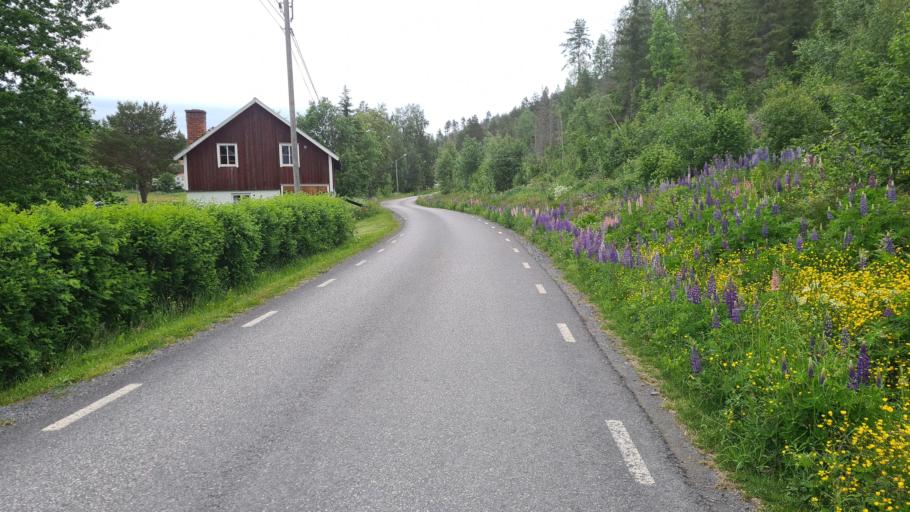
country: SE
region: Vaesternorrland
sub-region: Kramfors Kommun
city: Nordingra
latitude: 62.9753
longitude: 18.4252
